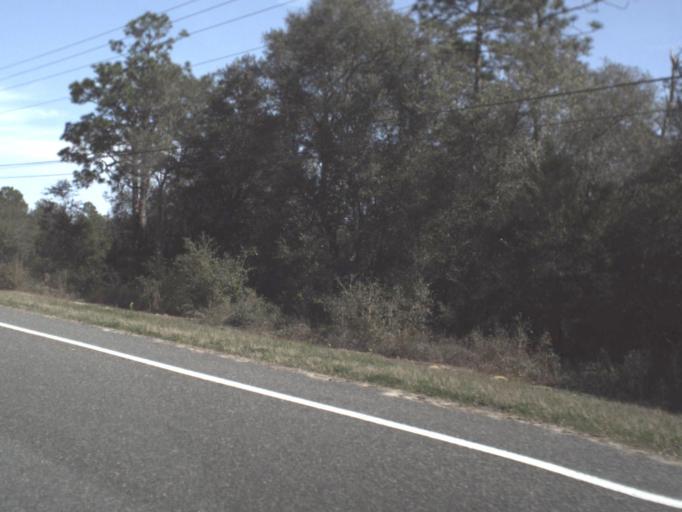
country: US
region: Florida
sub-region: Bay County
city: Lynn Haven
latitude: 30.4231
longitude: -85.6882
